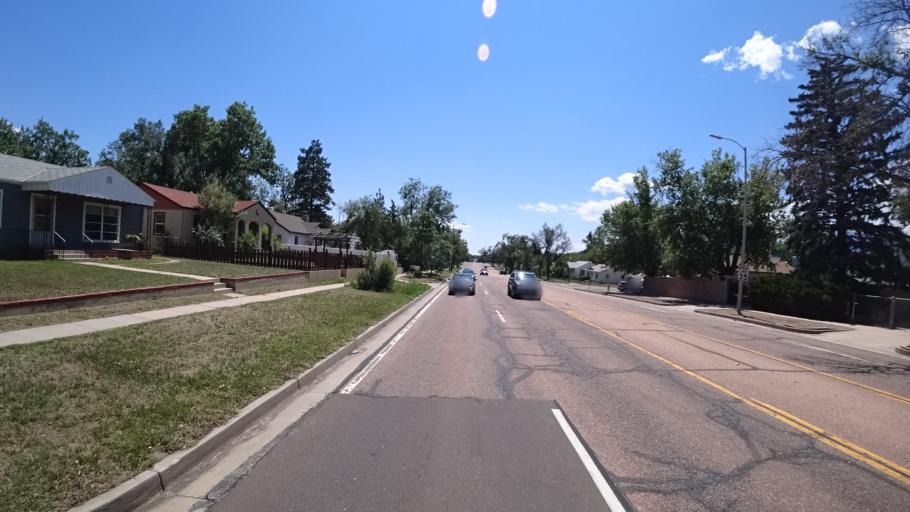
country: US
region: Colorado
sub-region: El Paso County
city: Colorado Springs
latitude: 38.8475
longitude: -104.7942
